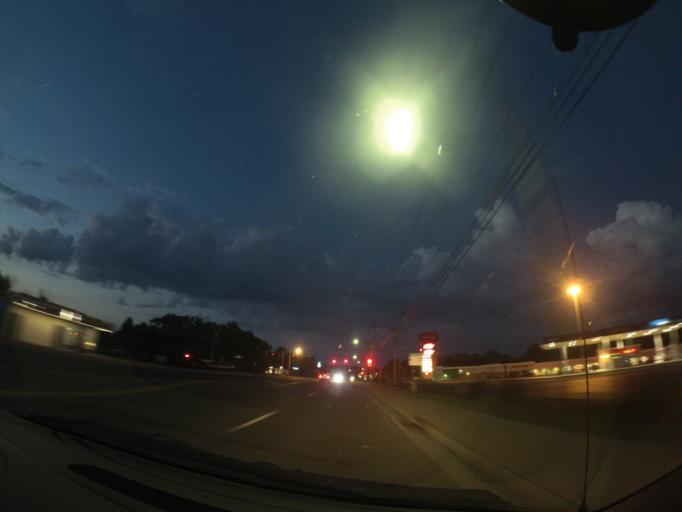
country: US
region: Ohio
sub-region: Ashtabula County
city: Ashtabula
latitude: 41.8540
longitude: -80.8181
